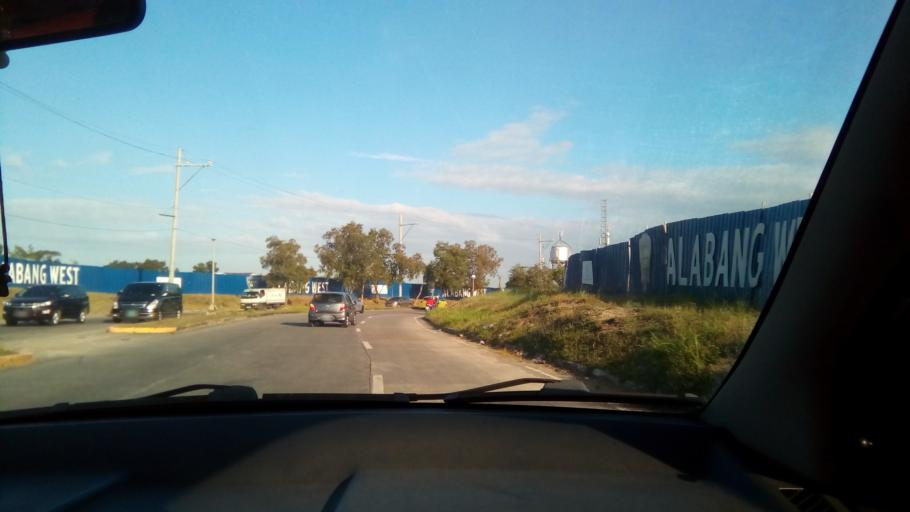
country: PH
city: Sambayanihan People's Village
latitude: 14.4051
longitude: 121.0124
